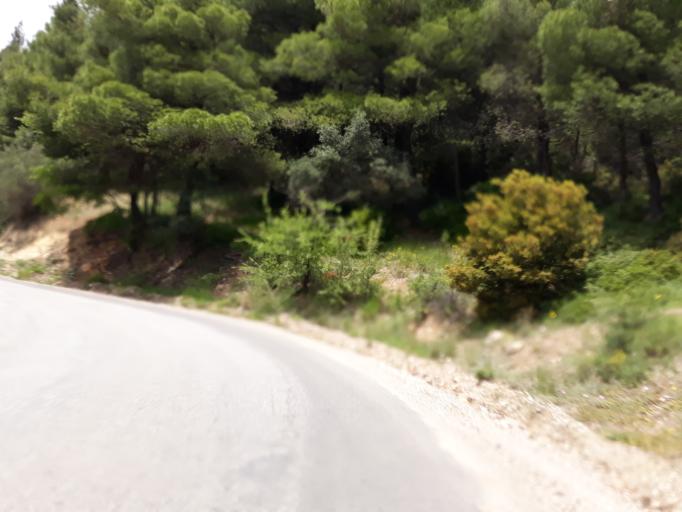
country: GR
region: Attica
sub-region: Nomarchia Dytikis Attikis
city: Magoula
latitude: 38.1530
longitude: 23.5175
